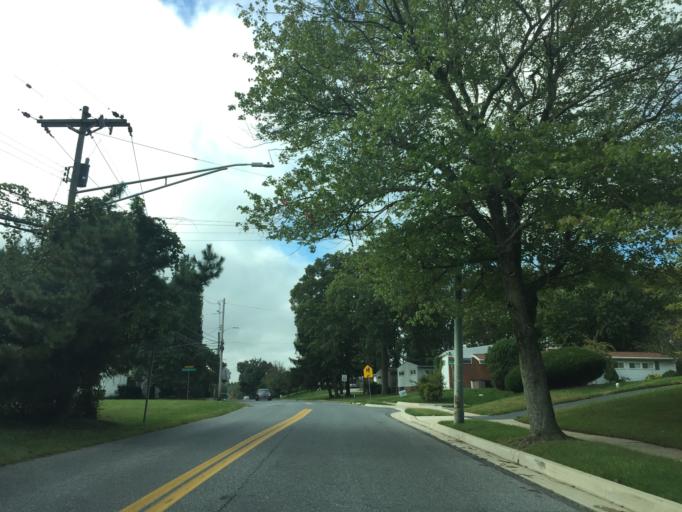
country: US
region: Maryland
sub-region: Baltimore County
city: Pikesville
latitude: 39.3779
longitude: -76.6764
